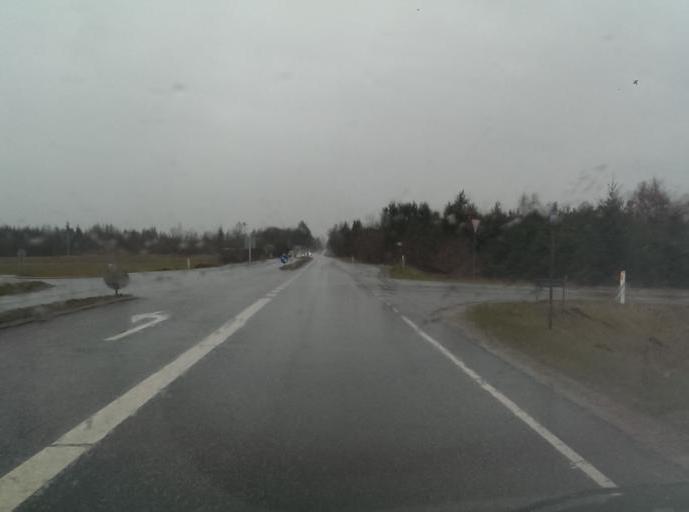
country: DK
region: Central Jutland
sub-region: Ringkobing-Skjern Kommune
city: Tarm
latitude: 55.8900
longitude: 8.5117
